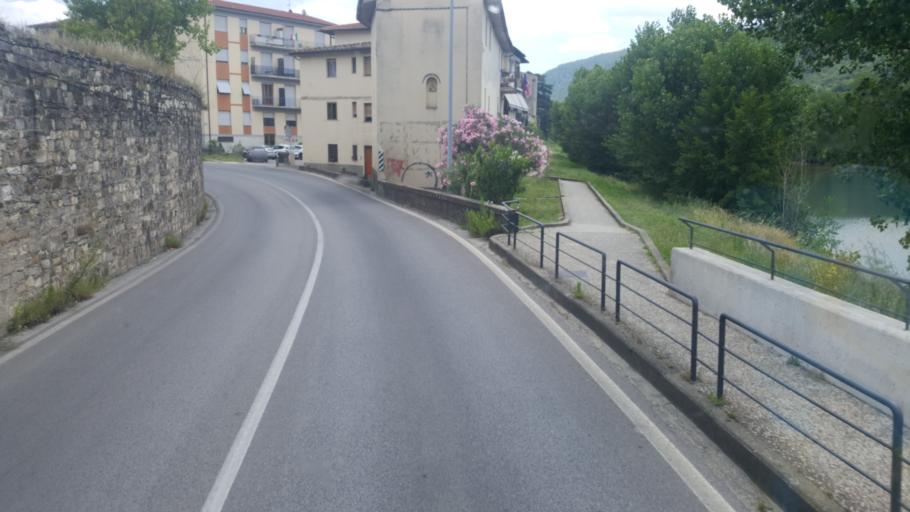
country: IT
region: Tuscany
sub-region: Province of Florence
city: Sieci
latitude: 43.7916
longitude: 11.3909
